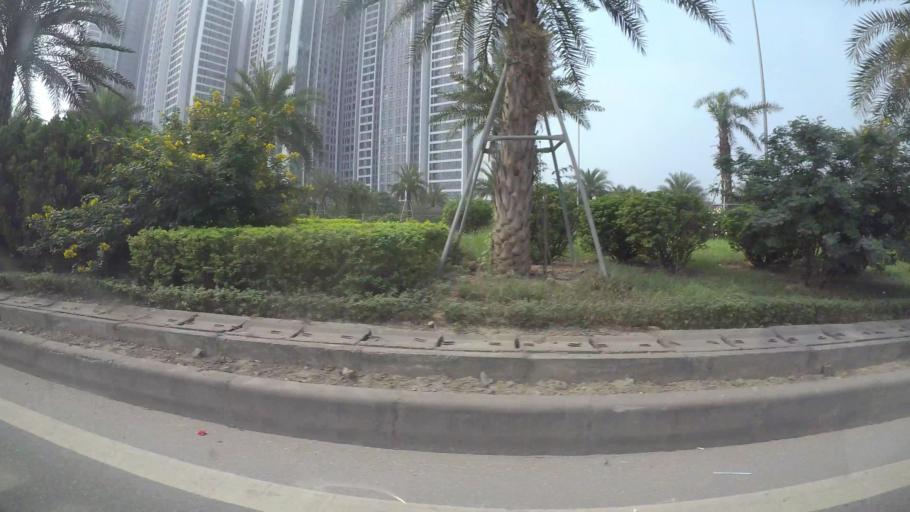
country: VN
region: Ha Noi
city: Thanh Xuan
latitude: 21.0025
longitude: 105.7828
